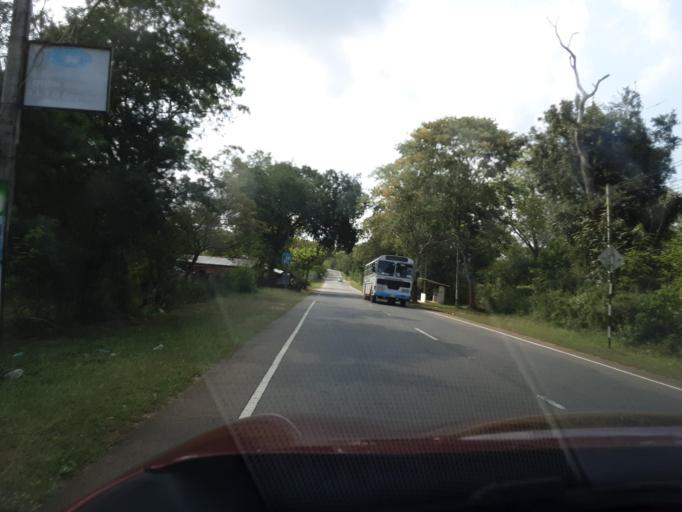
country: LK
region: Uva
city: Haputale
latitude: 6.3674
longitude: 81.1750
